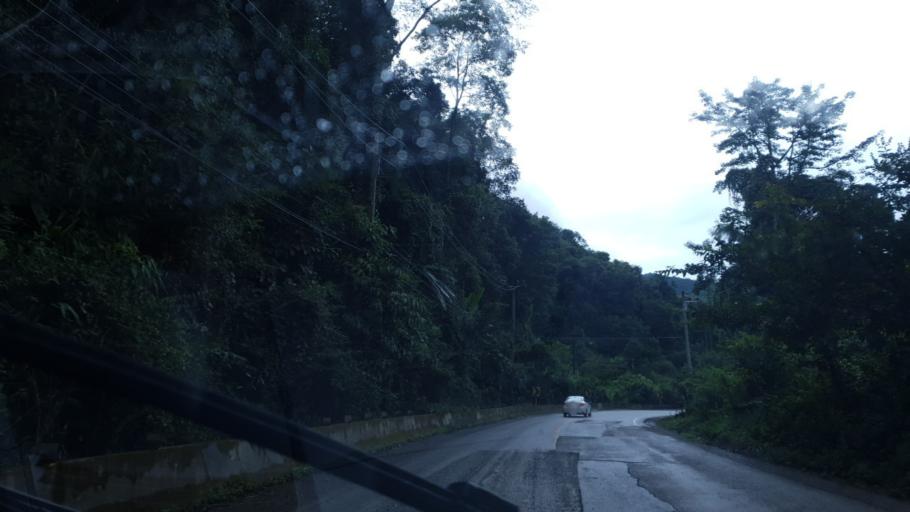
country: TH
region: Mae Hong Son
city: Ban Huai I Huak
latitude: 18.1513
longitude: 98.1247
